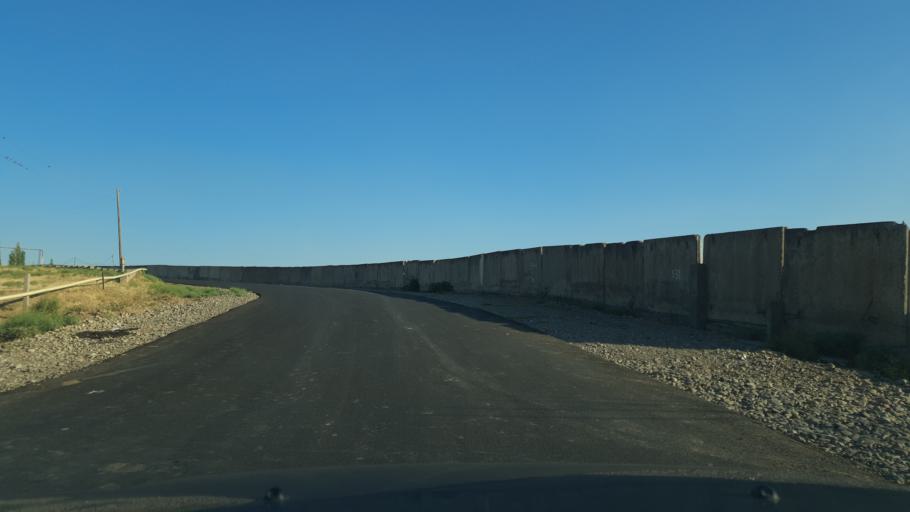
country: UZ
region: Toshkent
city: Salor
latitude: 41.4590
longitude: 69.3942
